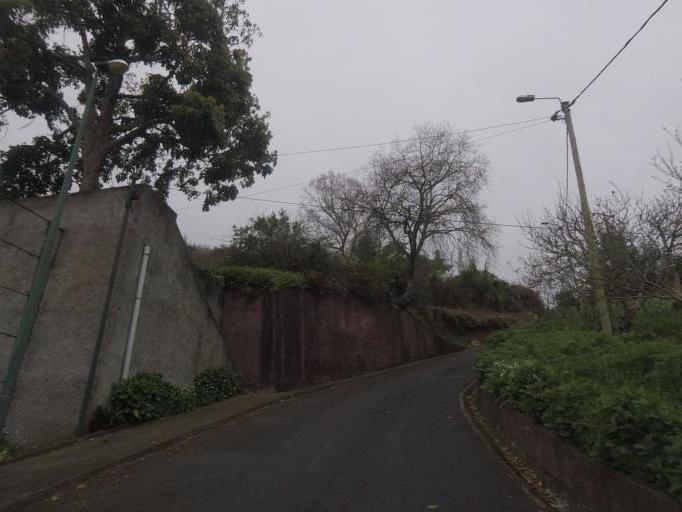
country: PT
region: Madeira
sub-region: Santa Cruz
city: Santa Cruz
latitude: 32.7346
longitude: -16.8217
